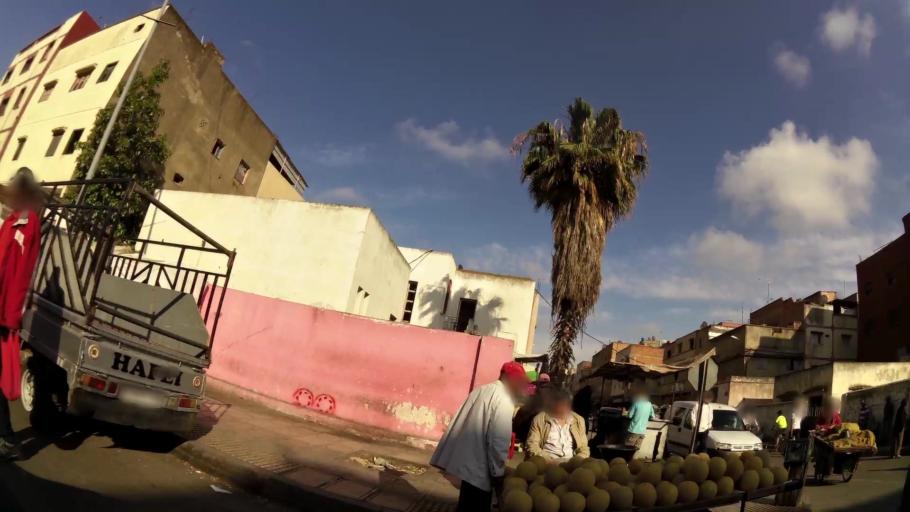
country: MA
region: Rabat-Sale-Zemmour-Zaer
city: Sale
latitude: 34.0533
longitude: -6.7809
